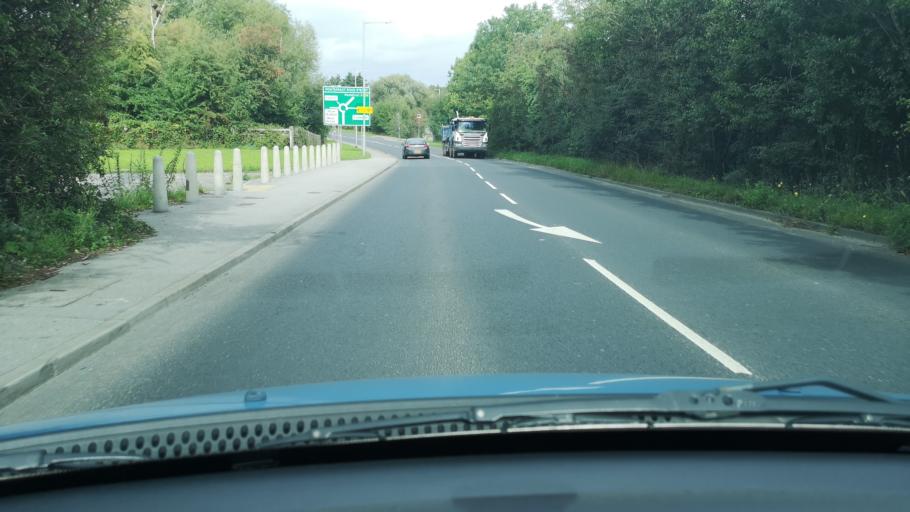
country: GB
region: England
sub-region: Barnsley
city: Cudworth
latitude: 53.5707
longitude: -1.4294
